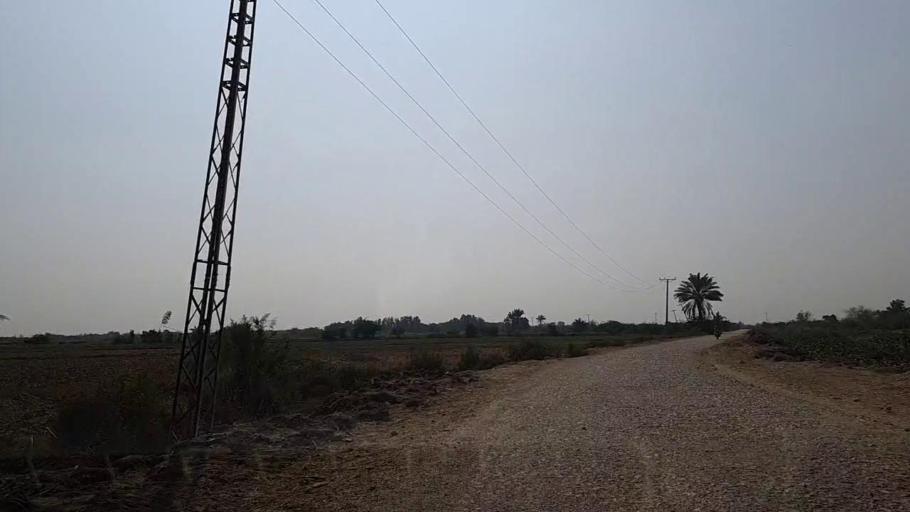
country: PK
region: Sindh
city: Thatta
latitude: 24.7365
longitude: 67.7702
